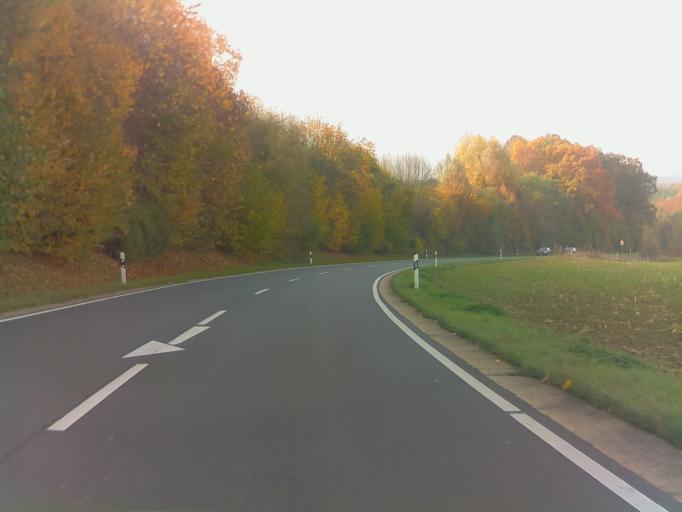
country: DE
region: Baden-Wuerttemberg
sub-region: Karlsruhe Region
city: Billigheim
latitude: 49.4063
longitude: 9.2490
